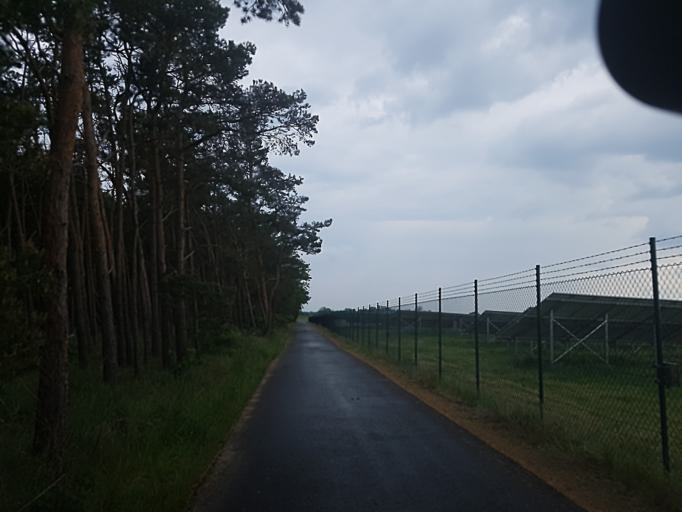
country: DE
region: Saxony-Anhalt
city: Elster
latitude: 51.8175
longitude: 12.8653
